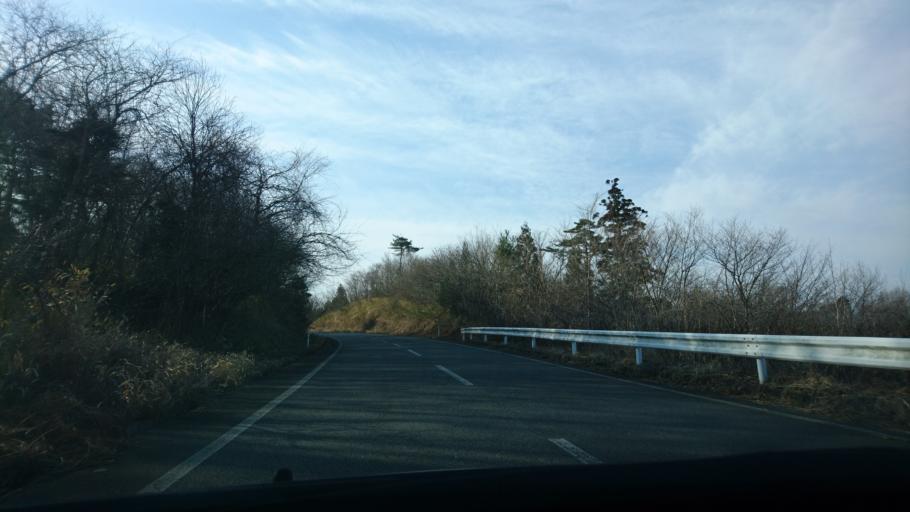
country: JP
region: Iwate
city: Ichinoseki
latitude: 38.8573
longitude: 141.2007
